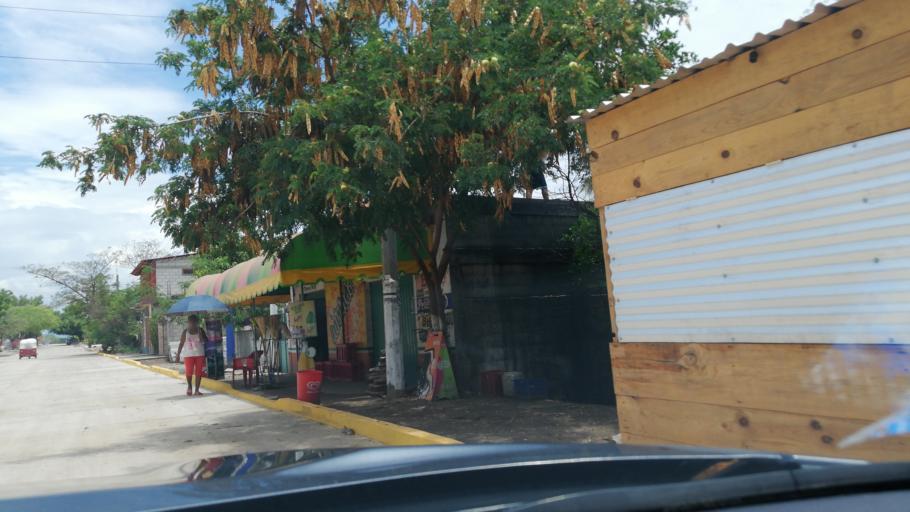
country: MX
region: Oaxaca
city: Santa Maria Jalapa del Marques
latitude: 16.4398
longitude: -95.4384
